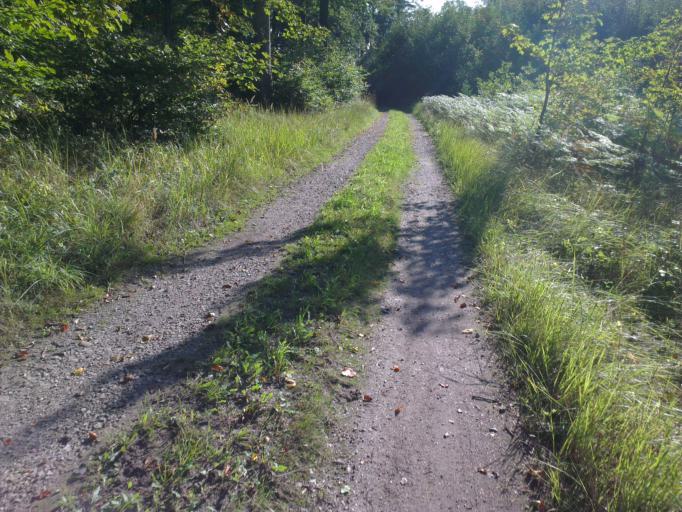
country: DK
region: Capital Region
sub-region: Frederikssund Kommune
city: Jaegerspris
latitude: 55.8752
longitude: 11.9928
